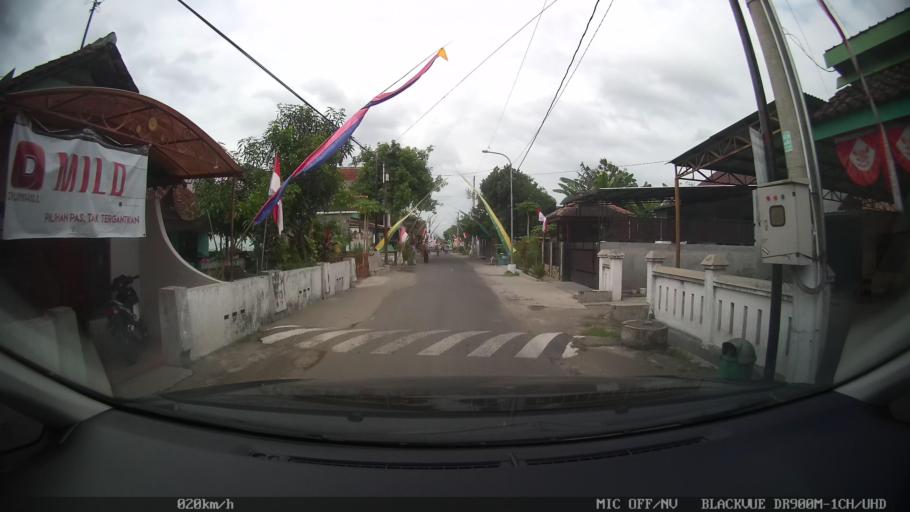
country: ID
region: Daerah Istimewa Yogyakarta
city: Depok
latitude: -7.8142
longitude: 110.4193
